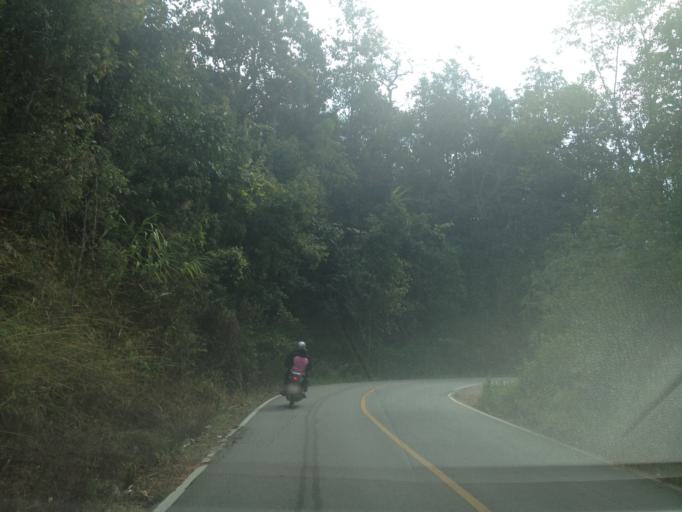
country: TH
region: Mae Hong Son
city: Ban Huai I Huak
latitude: 18.1276
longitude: 98.2184
